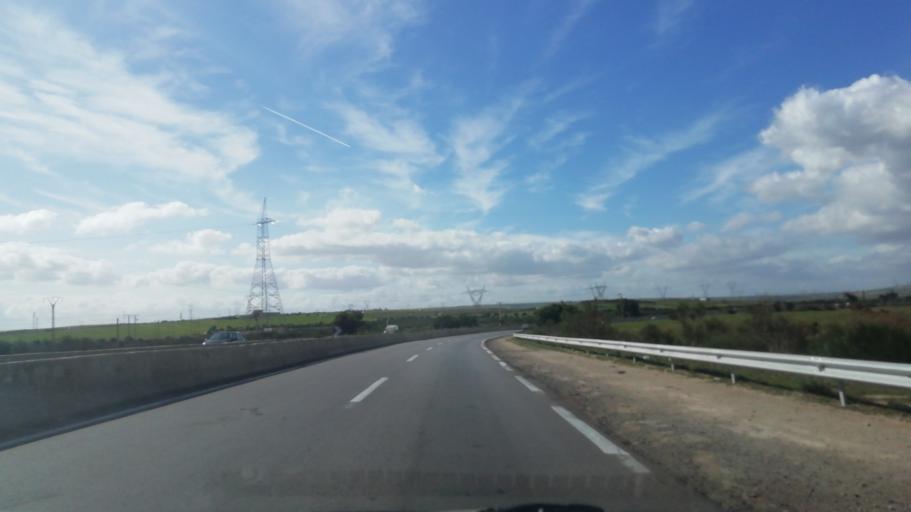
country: DZ
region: Oran
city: Ain el Bya
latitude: 35.7834
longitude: -0.1303
